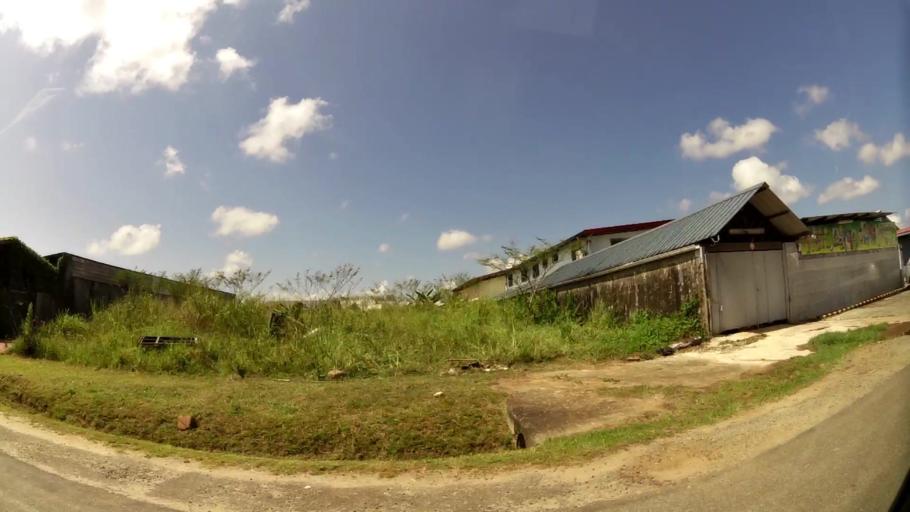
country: GF
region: Guyane
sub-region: Guyane
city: Cayenne
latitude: 4.9312
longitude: -52.3284
